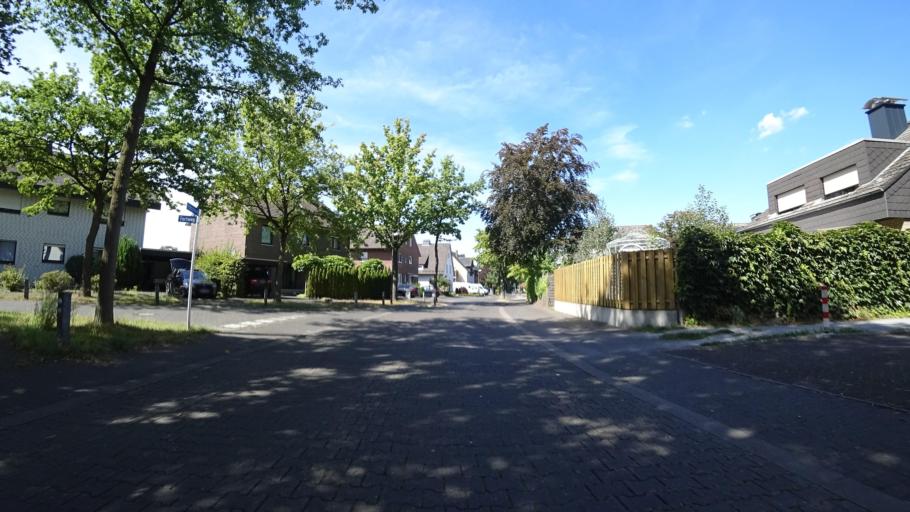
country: DE
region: North Rhine-Westphalia
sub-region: Regierungsbezirk Detmold
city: Guetersloh
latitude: 51.8913
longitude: 8.4033
